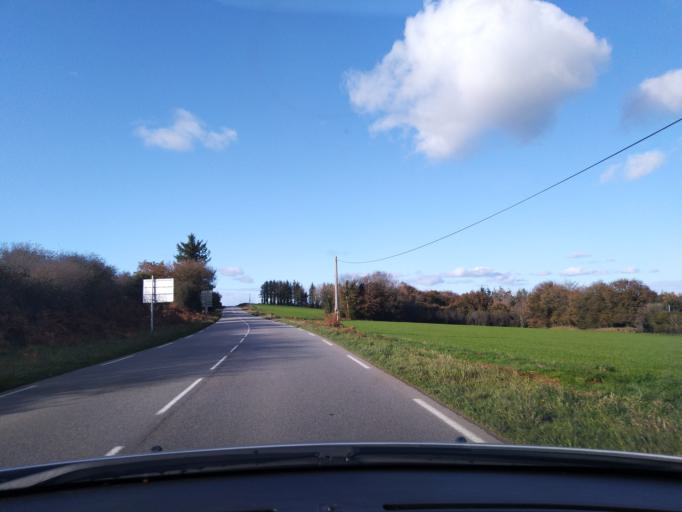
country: FR
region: Brittany
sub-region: Departement du Finistere
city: Guerlesquin
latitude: 48.5242
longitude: -3.5927
